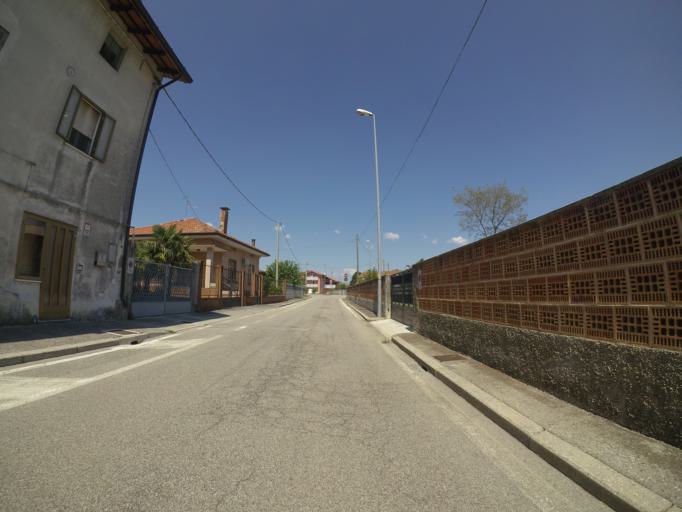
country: IT
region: Friuli Venezia Giulia
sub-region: Provincia di Udine
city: Mortegliano
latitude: 45.9443
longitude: 13.1676
